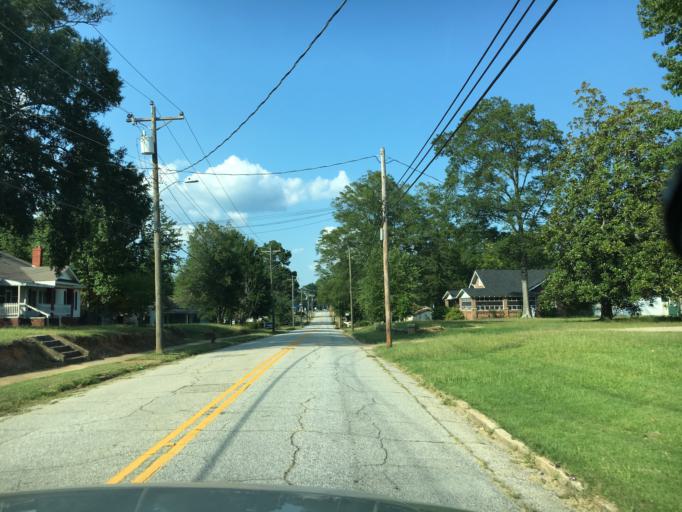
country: US
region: South Carolina
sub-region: Laurens County
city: Clinton
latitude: 34.4790
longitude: -81.8772
